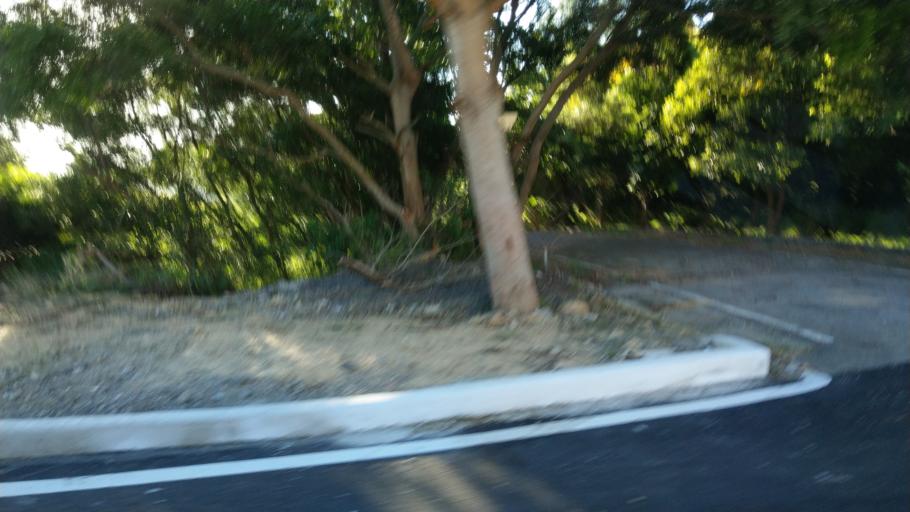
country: TW
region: Taiwan
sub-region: Miaoli
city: Miaoli
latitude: 24.5387
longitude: 120.7917
